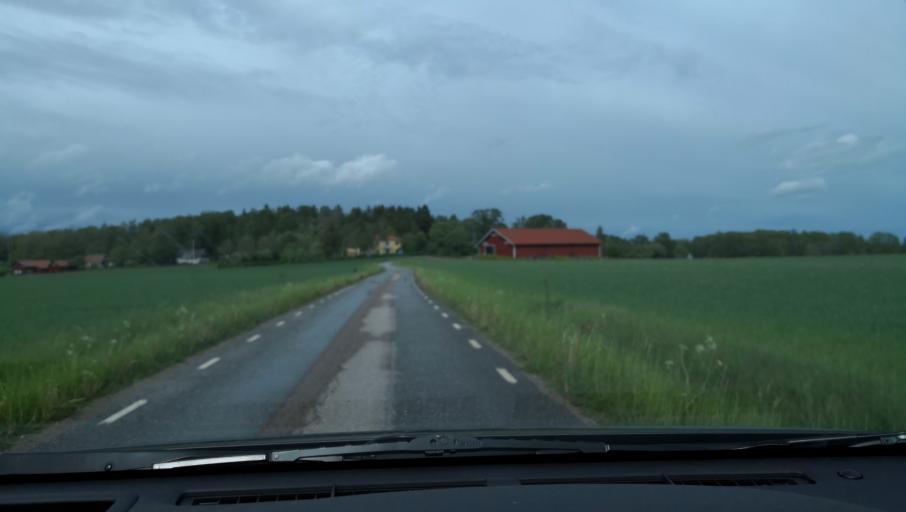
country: SE
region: Uppsala
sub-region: Enkopings Kommun
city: Orsundsbro
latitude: 59.7179
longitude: 17.4247
